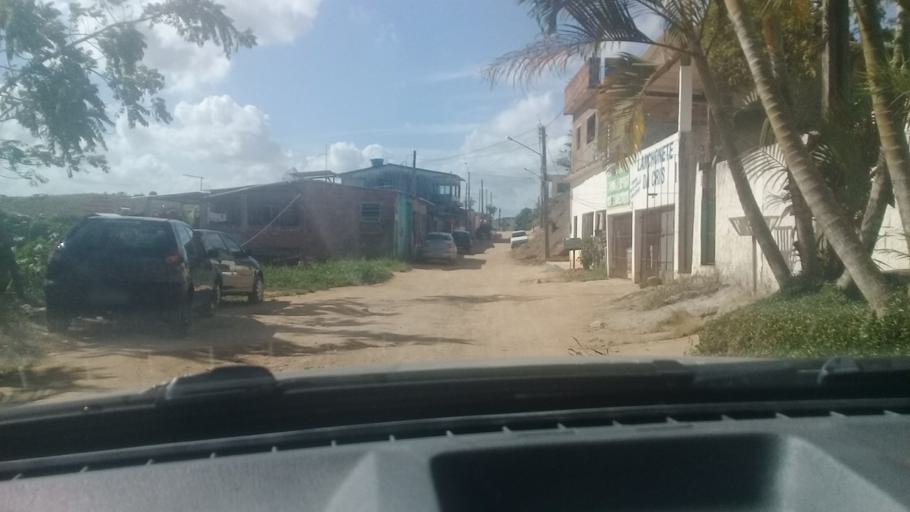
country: BR
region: Pernambuco
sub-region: Jaboatao Dos Guararapes
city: Jaboatao dos Guararapes
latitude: -8.0883
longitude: -35.0298
